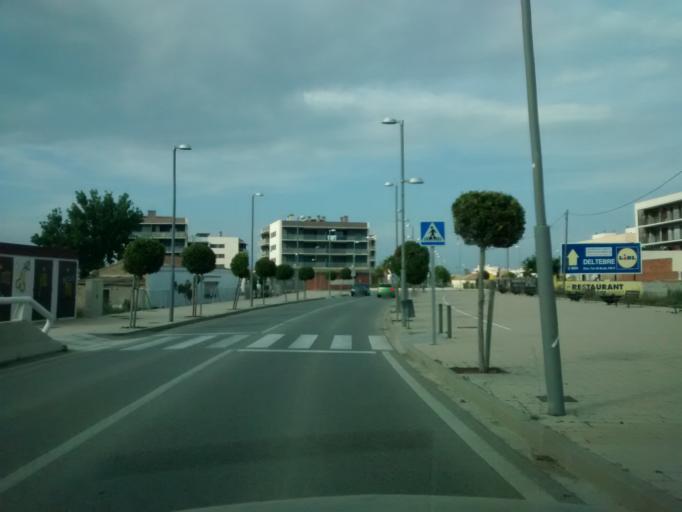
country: ES
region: Catalonia
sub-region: Provincia de Tarragona
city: Deltebre
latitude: 40.7147
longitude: 0.7182
